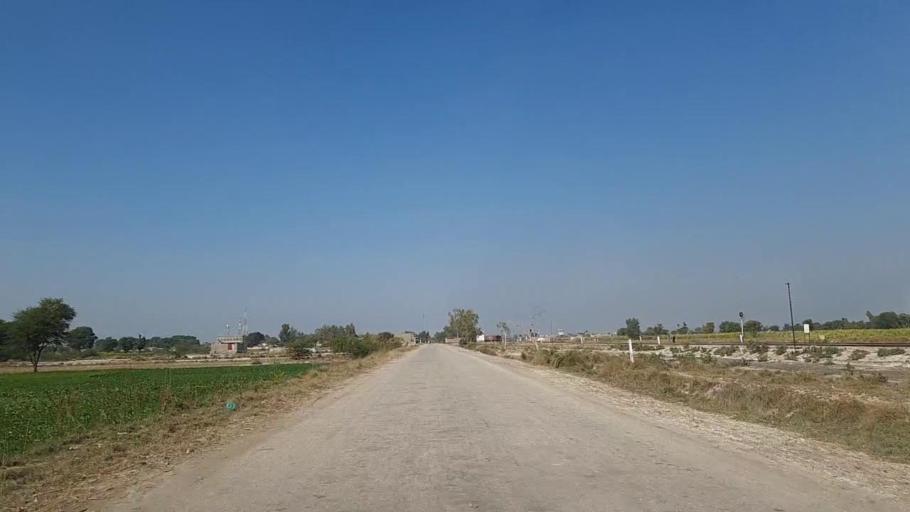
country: PK
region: Sindh
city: Nawabshah
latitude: 26.3455
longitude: 68.3687
